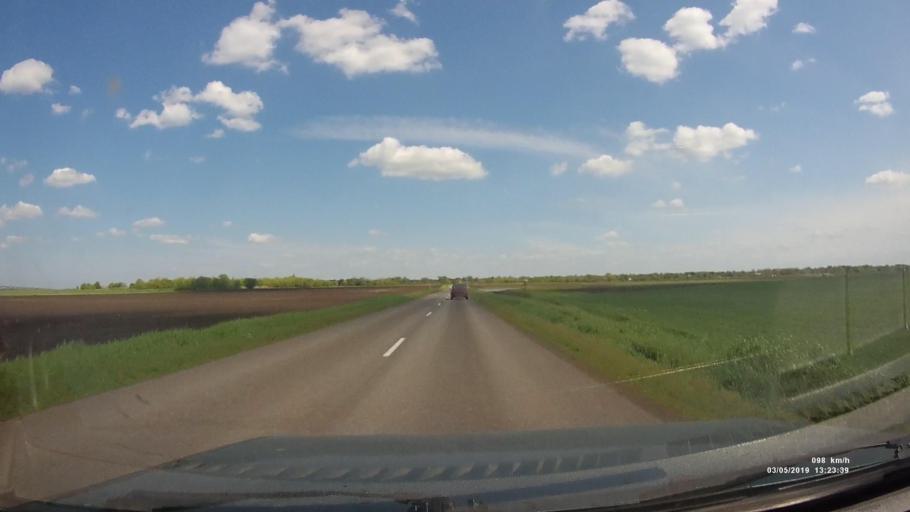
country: RU
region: Rostov
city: Semikarakorsk
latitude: 47.5625
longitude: 40.7866
